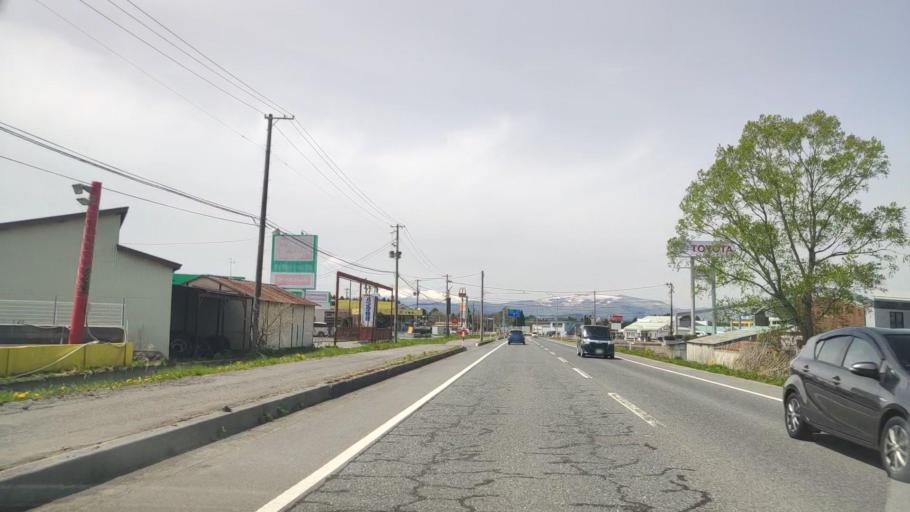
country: JP
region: Aomori
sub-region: Misawa Shi
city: Inuotose
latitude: 40.6440
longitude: 141.2017
